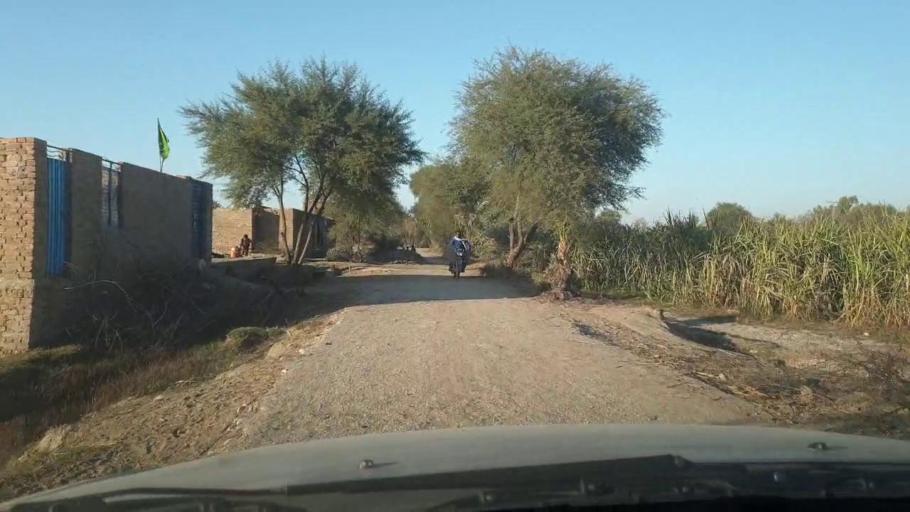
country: PK
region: Sindh
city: Ghotki
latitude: 28.0258
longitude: 69.3081
